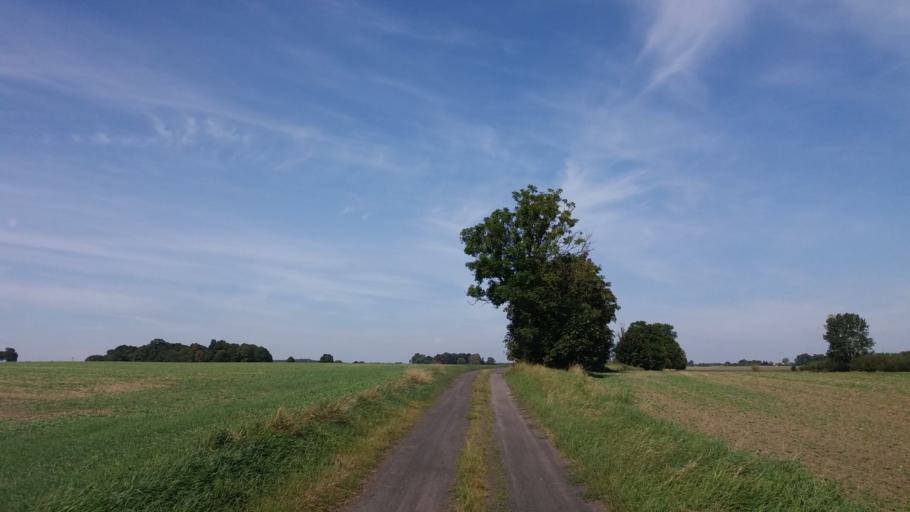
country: PL
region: West Pomeranian Voivodeship
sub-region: Powiat choszczenski
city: Choszczno
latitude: 53.1323
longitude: 15.4051
